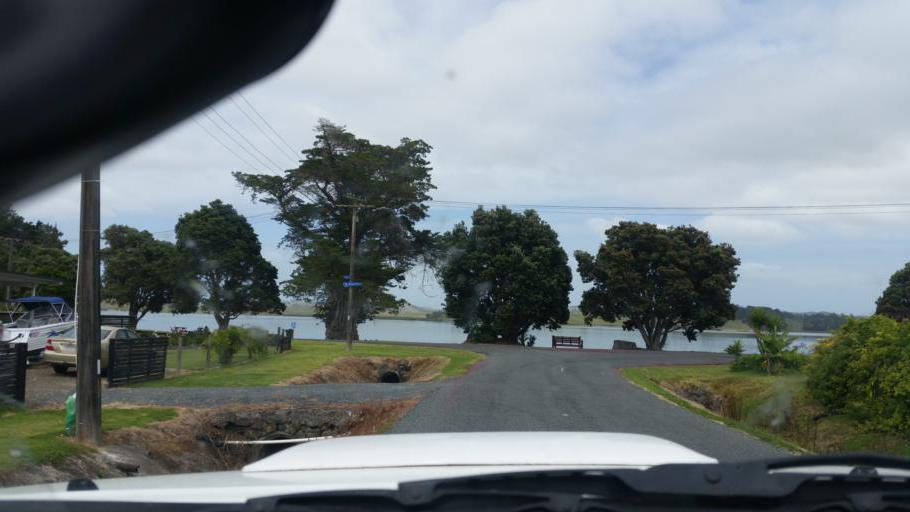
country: NZ
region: Auckland
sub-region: Auckland
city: Wellsford
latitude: -36.1587
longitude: 174.2379
